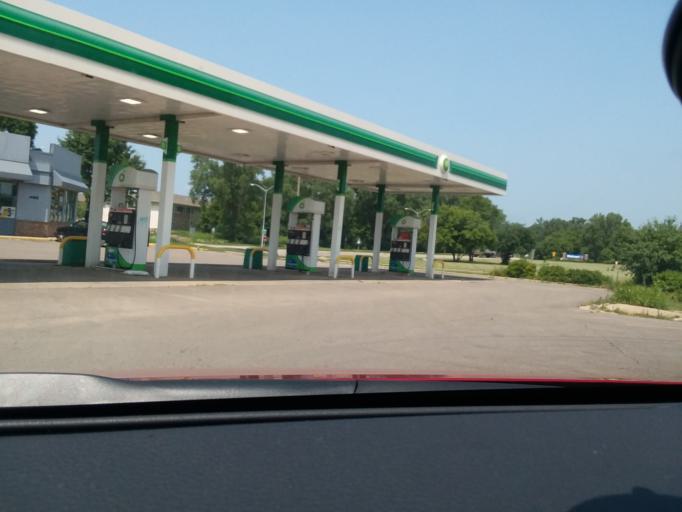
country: US
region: Wisconsin
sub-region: Dane County
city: Monona
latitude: 43.1081
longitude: -89.3138
